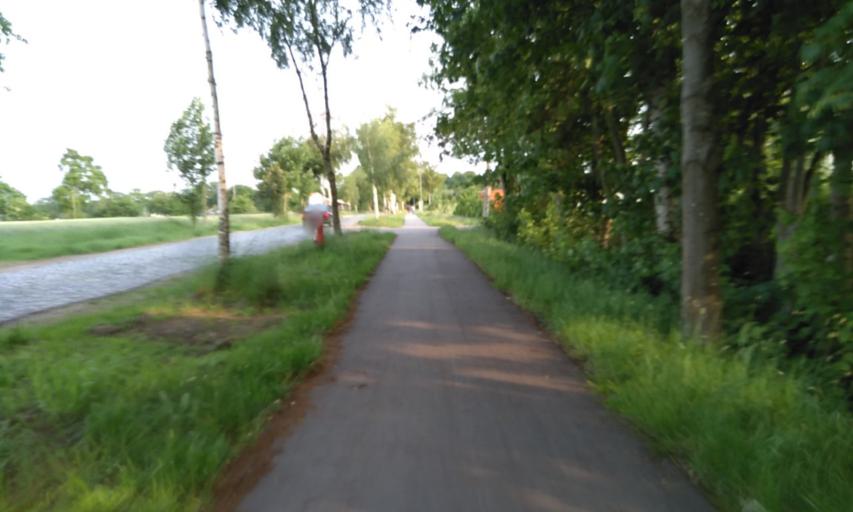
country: DE
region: Lower Saxony
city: Deinste
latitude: 53.5229
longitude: 9.4432
